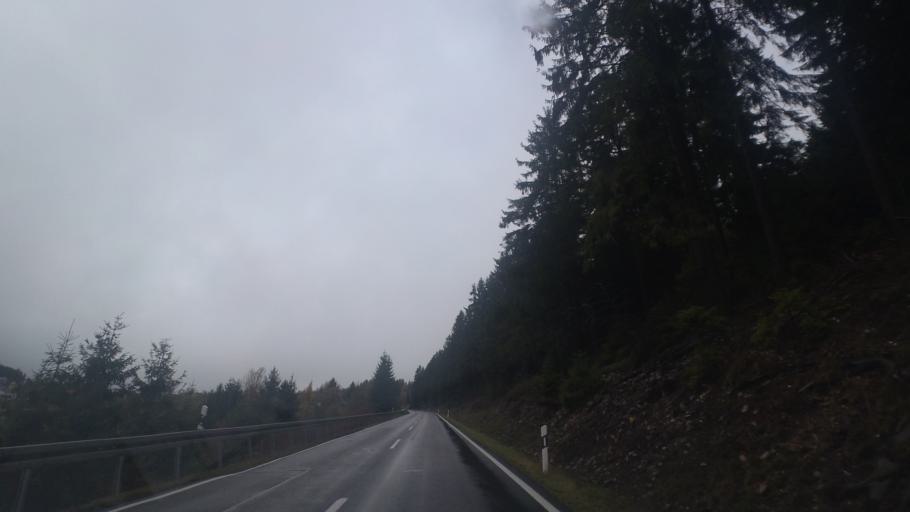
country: DE
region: Thuringia
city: Steinheid
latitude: 50.4774
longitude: 11.0887
